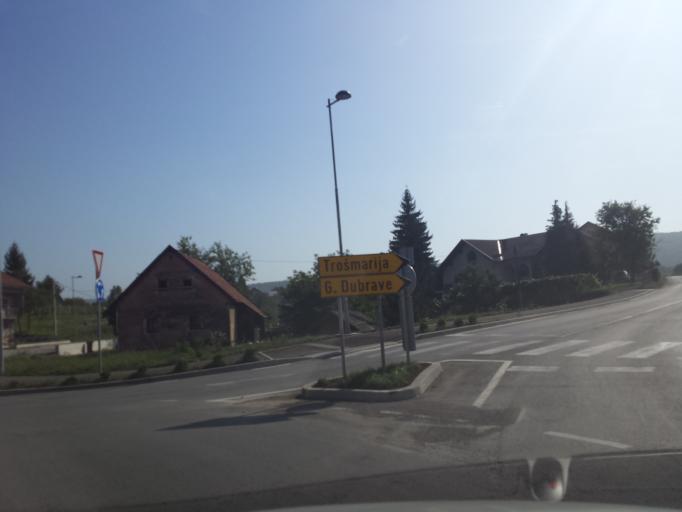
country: HR
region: Karlovacka
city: Ostarije
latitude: 45.2516
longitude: 15.3375
